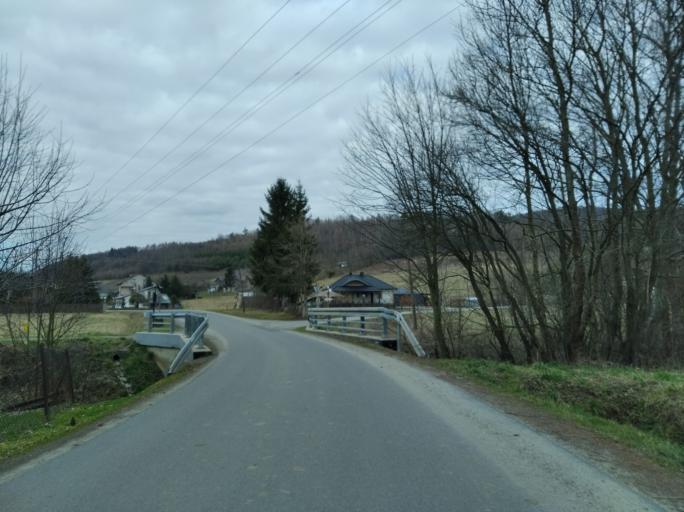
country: PL
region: Subcarpathian Voivodeship
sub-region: Powiat strzyzowski
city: Frysztak
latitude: 49.8442
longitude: 21.6277
